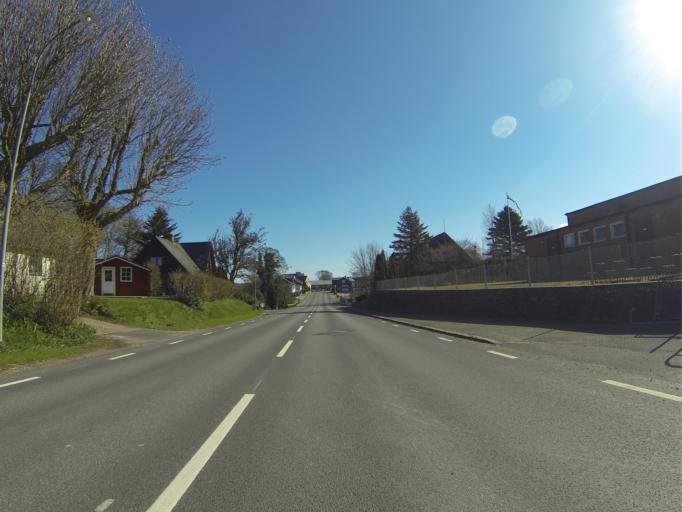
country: SE
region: Skane
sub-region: Tomelilla Kommun
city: Tomelilla
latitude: 55.5800
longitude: 14.0126
